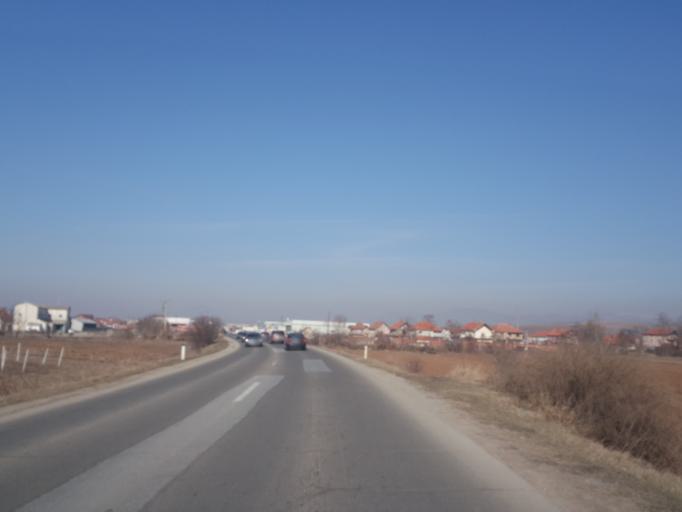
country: XK
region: Mitrovica
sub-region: Vushtrri
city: Vushtrri
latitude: 42.7802
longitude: 21.0135
